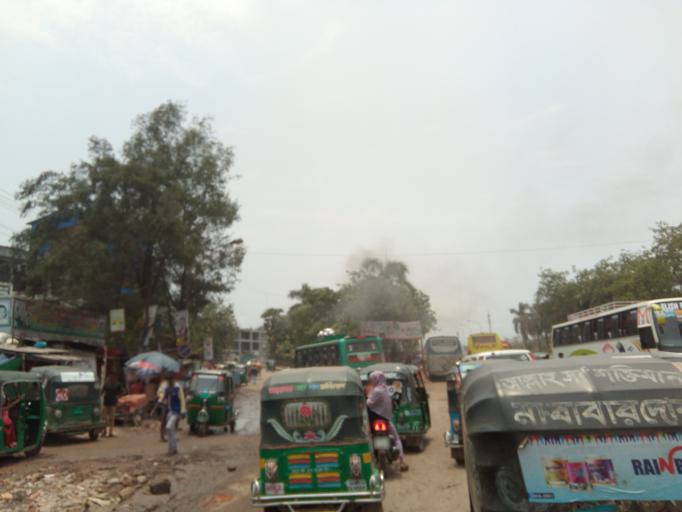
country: BD
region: Dhaka
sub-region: Dhaka
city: Dhaka
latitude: 23.6921
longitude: 90.4327
